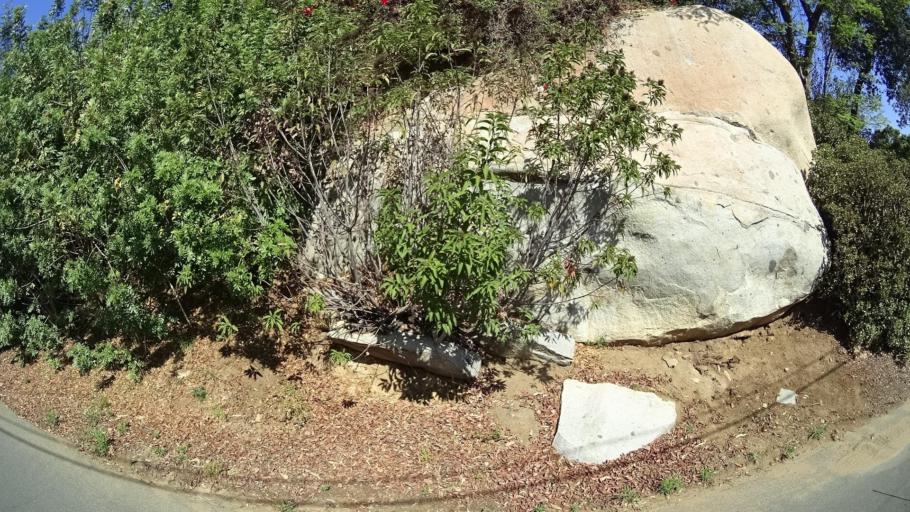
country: US
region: California
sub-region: San Diego County
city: Casa de Oro-Mount Helix
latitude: 32.7743
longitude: -116.9862
